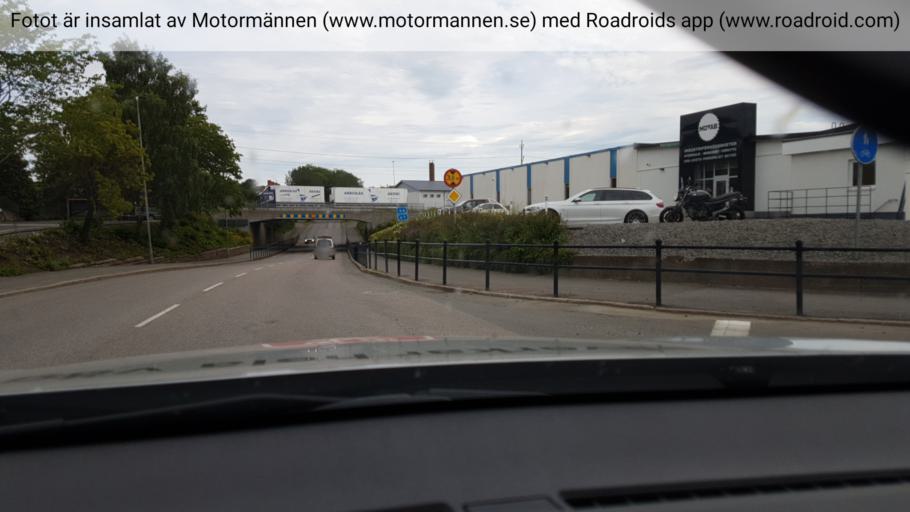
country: SE
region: Vaestra Goetaland
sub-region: Falkopings Kommun
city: Falkoeping
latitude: 58.1665
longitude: 13.5430
